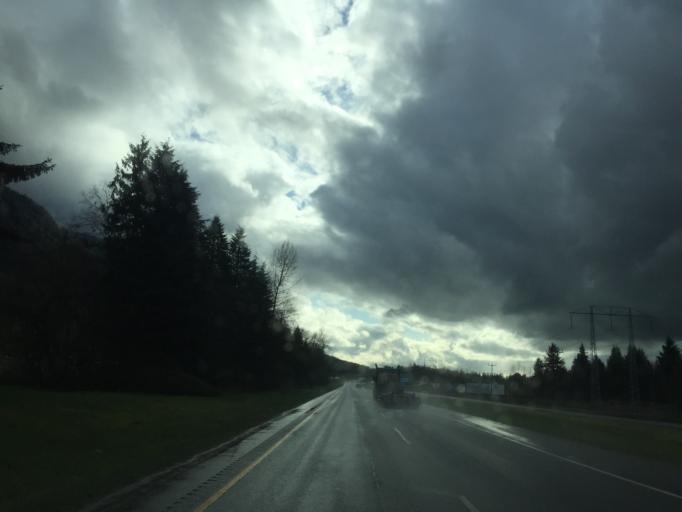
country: CA
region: British Columbia
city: Agassiz
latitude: 49.2039
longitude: -121.7196
